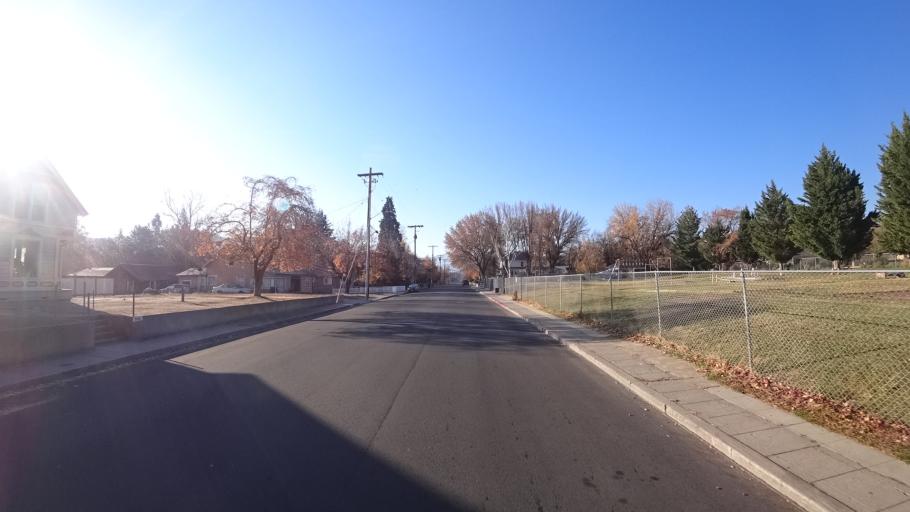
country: US
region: California
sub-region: Siskiyou County
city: Yreka
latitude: 41.7383
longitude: -122.6362
